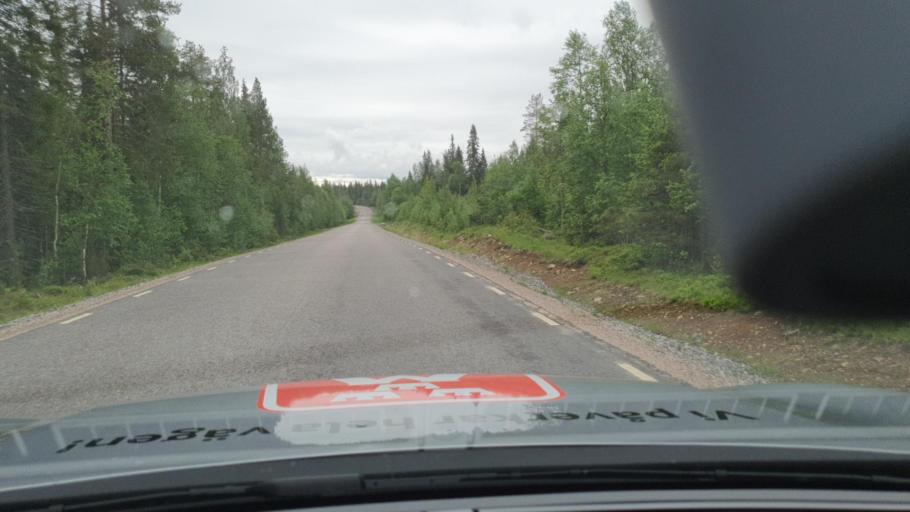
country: SE
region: Norrbotten
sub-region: Overtornea Kommun
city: OEvertornea
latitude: 66.5010
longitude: 23.4232
